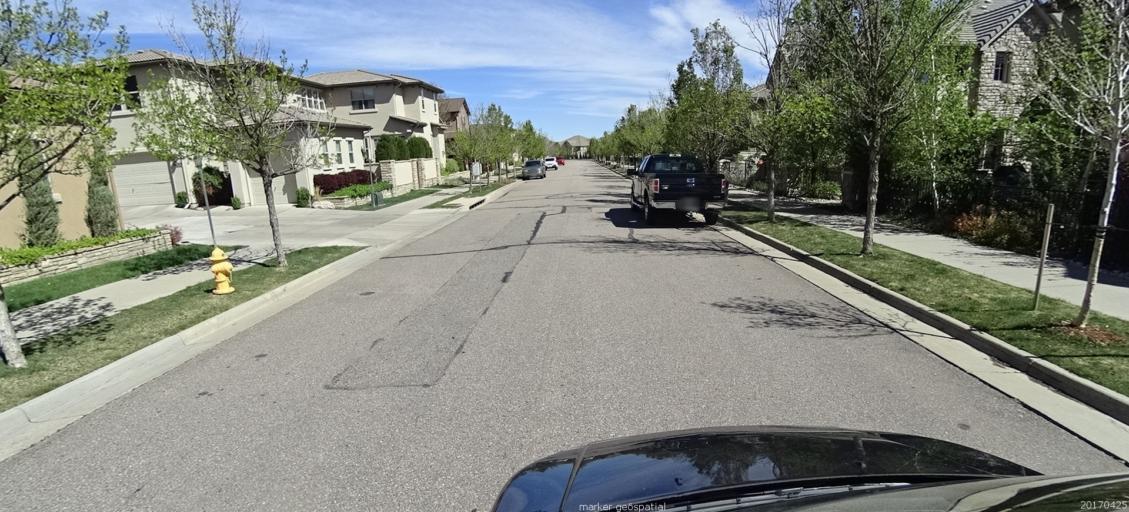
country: US
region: Colorado
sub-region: Douglas County
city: Carriage Club
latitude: 39.5299
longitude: -104.8848
